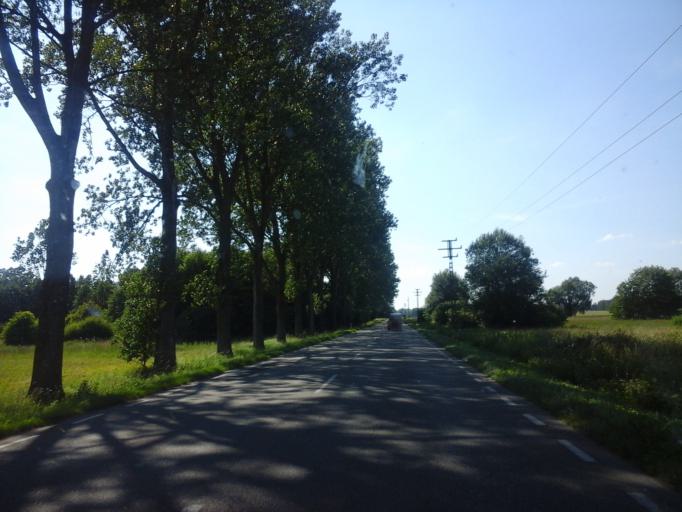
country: PL
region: West Pomeranian Voivodeship
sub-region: Powiat bialogardzki
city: Karlino
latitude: 54.0246
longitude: 15.9270
